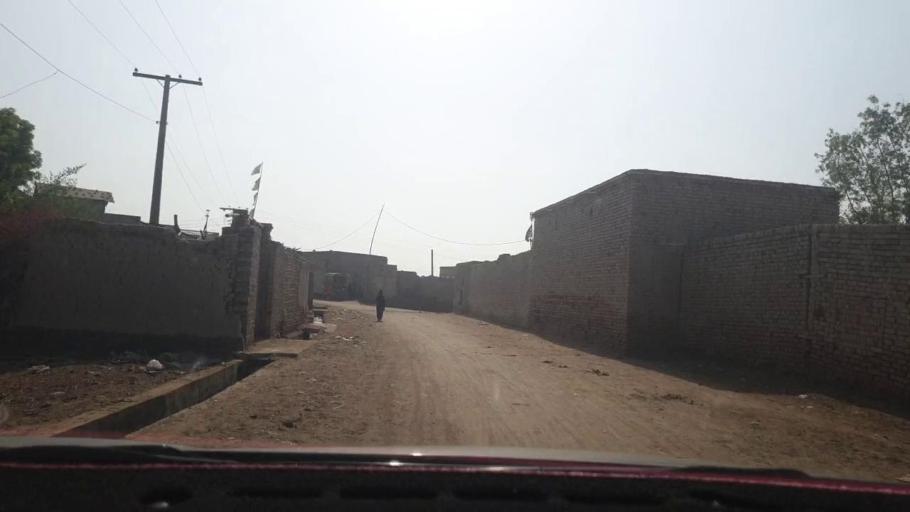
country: PK
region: Sindh
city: Nasirabad
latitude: 27.4383
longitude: 67.9561
